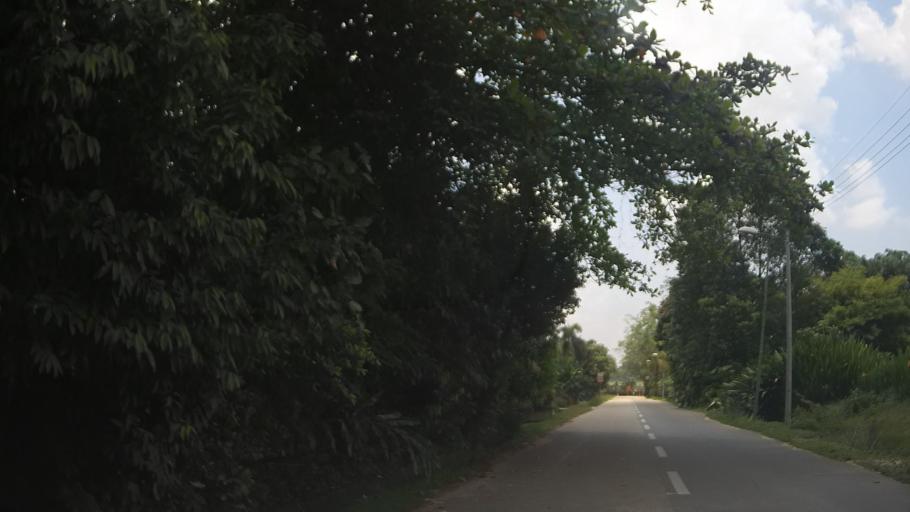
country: MY
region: Johor
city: Kampung Pasir Gudang Baru
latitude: 1.3975
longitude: 103.8637
